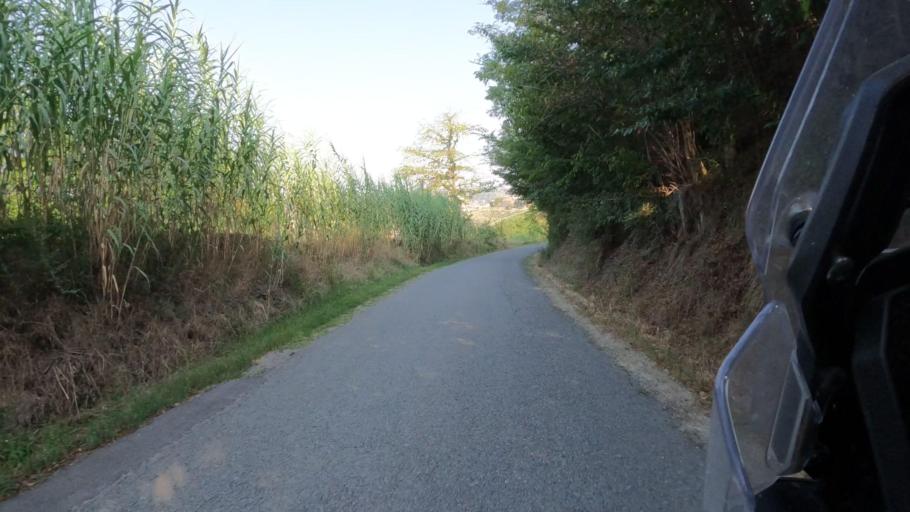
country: IT
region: Piedmont
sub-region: Provincia di Asti
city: Nizza Monferrato
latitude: 44.7620
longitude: 8.3780
